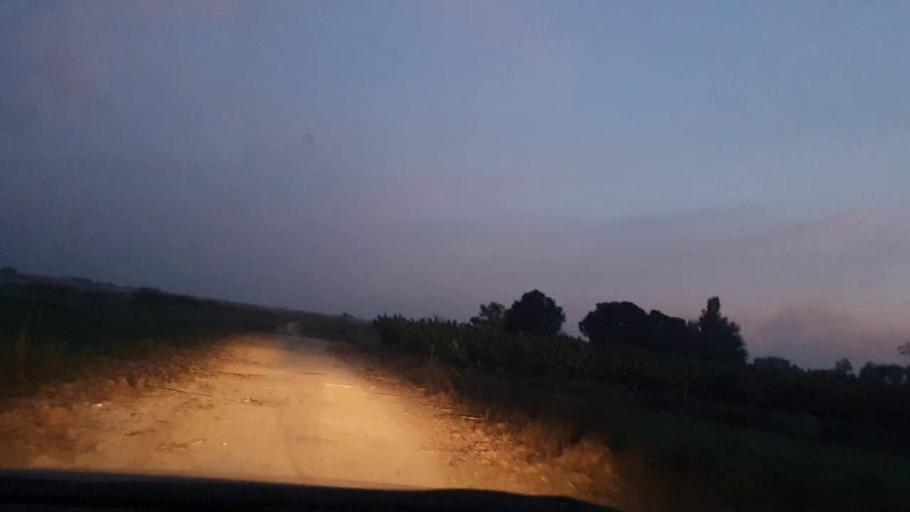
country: PK
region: Sindh
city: Sakrand
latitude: 26.1843
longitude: 68.3057
